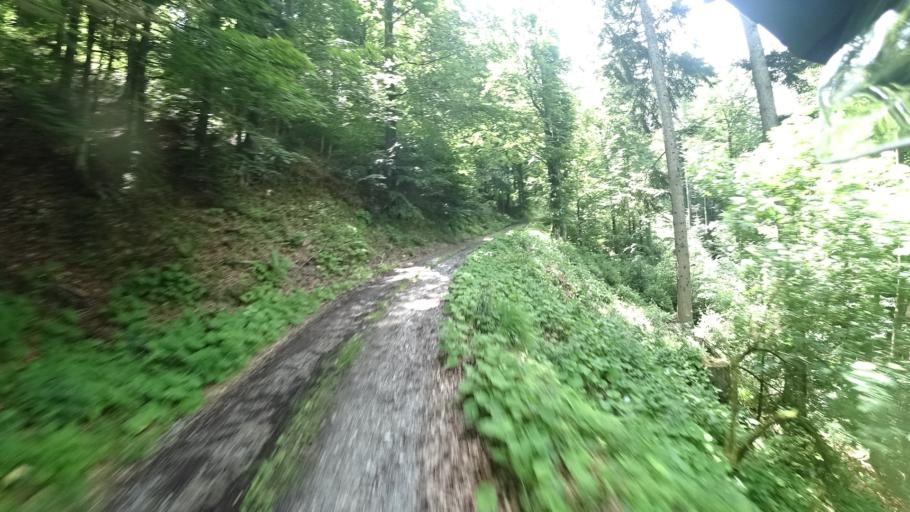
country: SI
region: Osilnica
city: Osilnica
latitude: 45.4678
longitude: 14.7292
